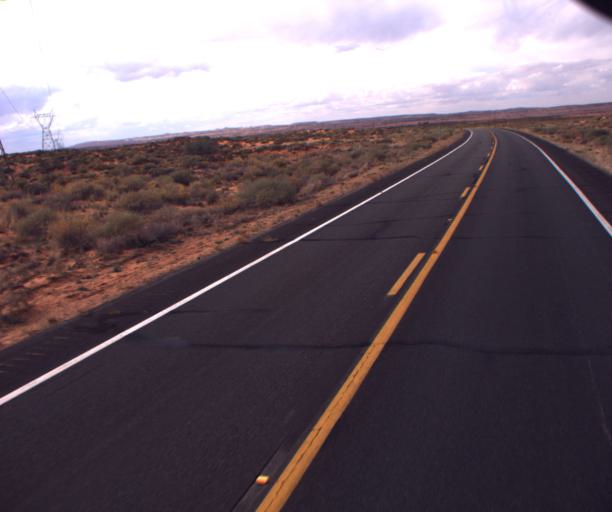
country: US
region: Arizona
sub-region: Apache County
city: Many Farms
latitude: 36.9396
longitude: -109.6406
